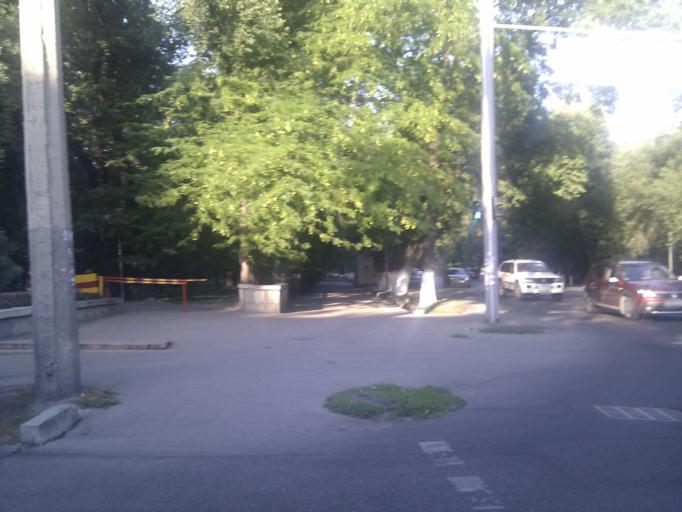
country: KZ
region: Almaty Qalasy
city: Almaty
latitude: 43.2569
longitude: 76.9504
